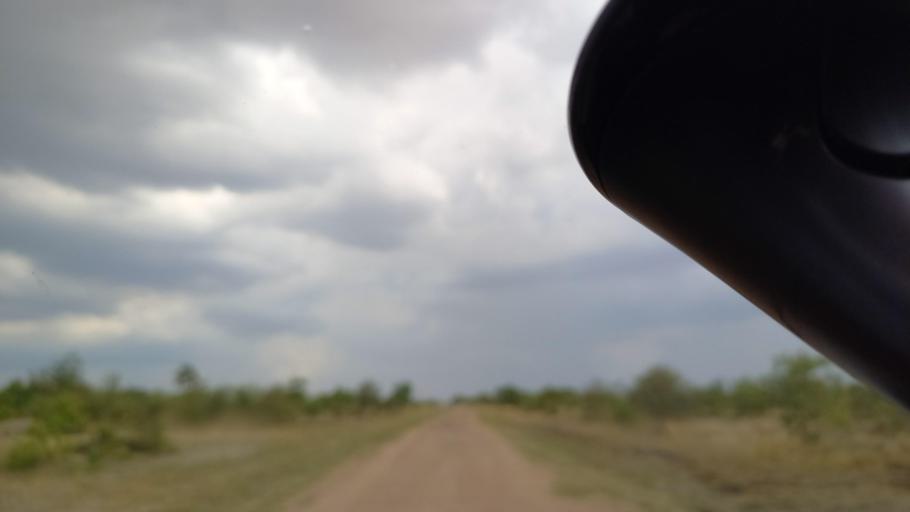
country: ZM
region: Lusaka
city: Kafue
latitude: -15.8407
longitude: 28.0902
